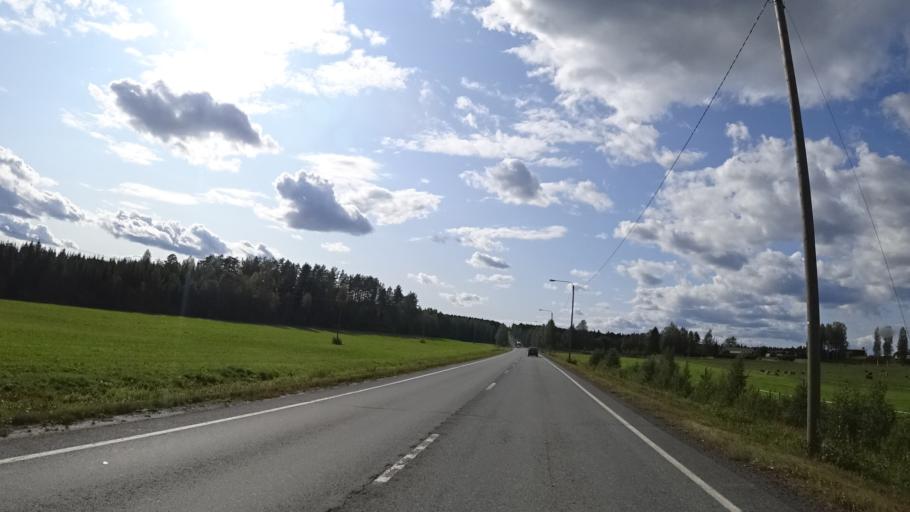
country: FI
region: North Karelia
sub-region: Keski-Karjala
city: Tohmajaervi
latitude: 62.2212
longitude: 30.3881
